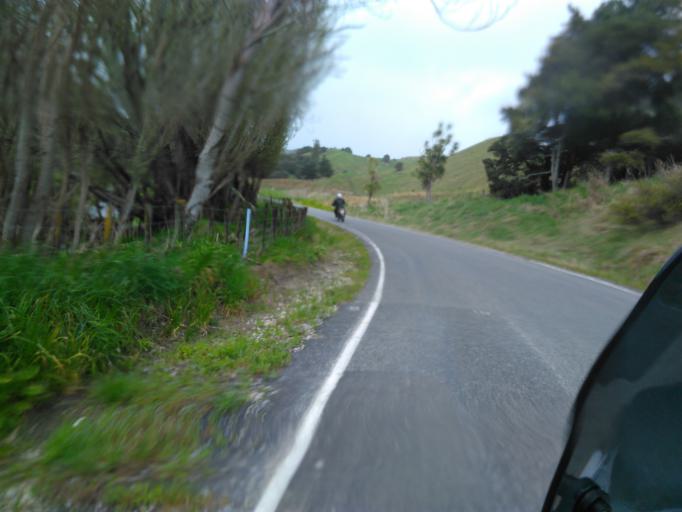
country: NZ
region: Gisborne
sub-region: Gisborne District
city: Gisborne
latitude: -38.6373
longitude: 177.7002
